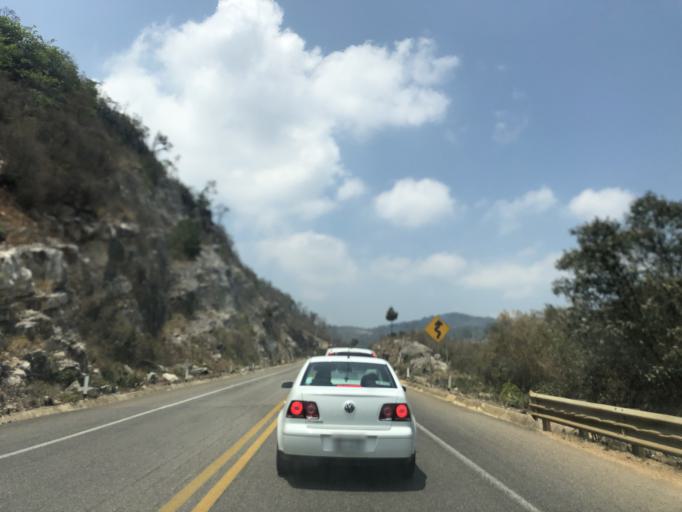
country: MX
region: Chiapas
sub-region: Zinacantan
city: Nachig
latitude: 16.6926
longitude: -92.7088
